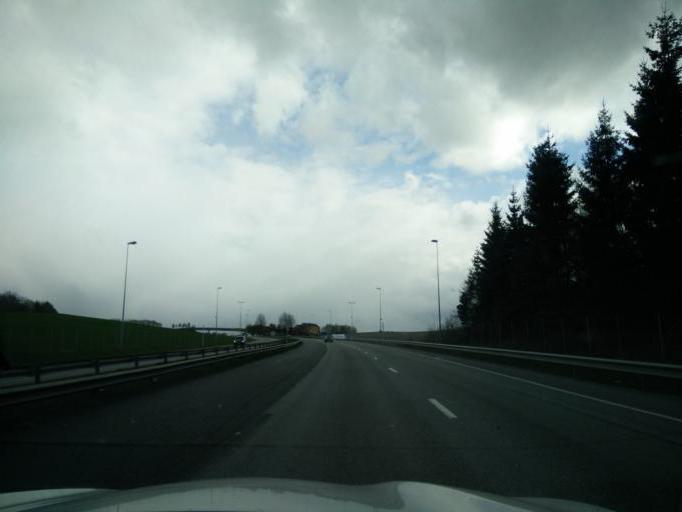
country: NO
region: Sor-Trondelag
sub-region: Trondheim
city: Trondheim
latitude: 63.3797
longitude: 10.3745
